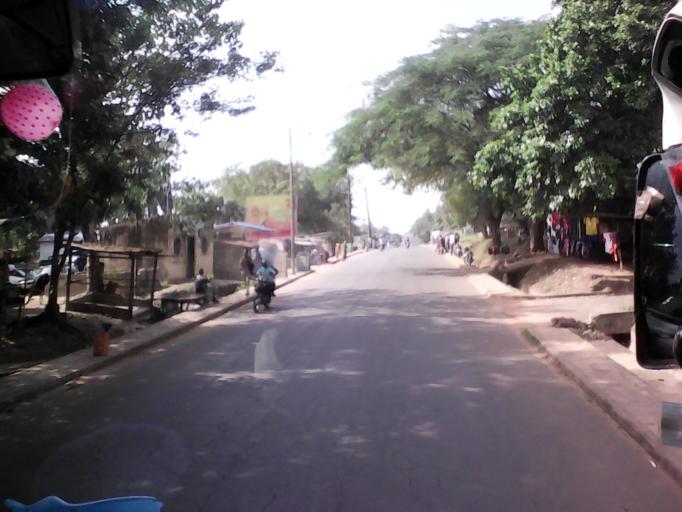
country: TG
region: Centrale
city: Sokode
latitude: 8.9768
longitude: 1.1391
